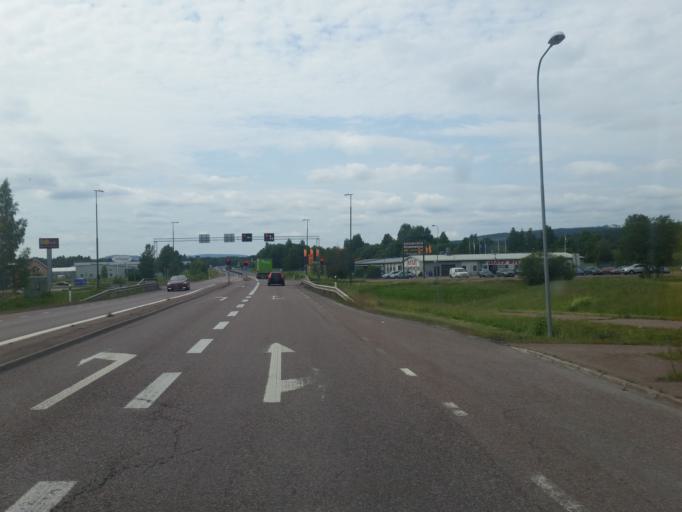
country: SE
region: Dalarna
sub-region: Borlange Kommun
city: Borlaenge
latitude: 60.4774
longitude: 15.4083
